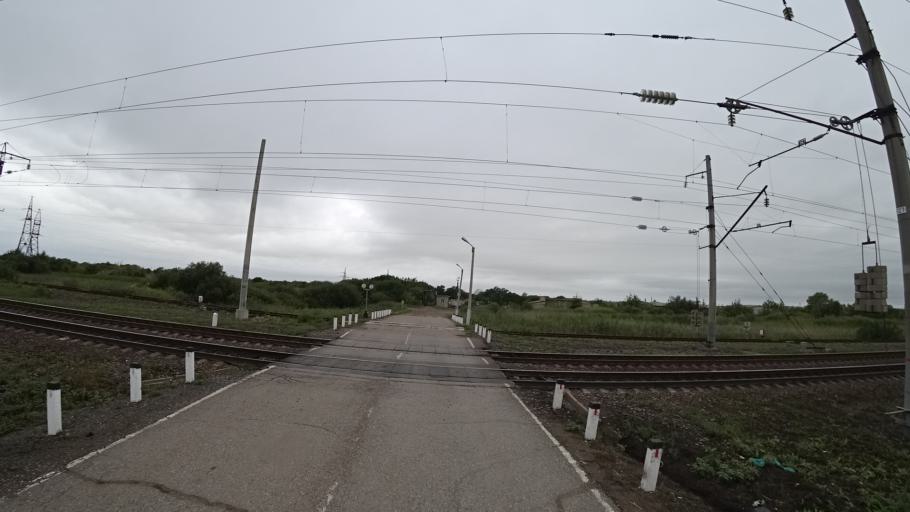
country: RU
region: Primorskiy
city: Chernigovka
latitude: 44.3332
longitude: 132.5235
